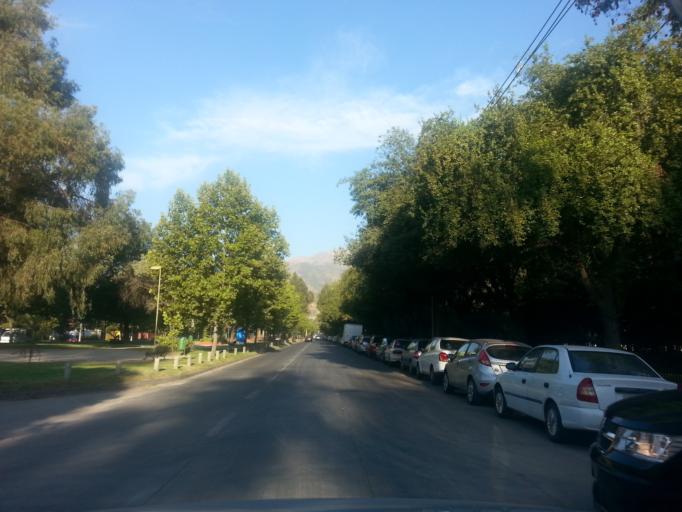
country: CL
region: Santiago Metropolitan
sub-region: Provincia de Santiago
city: Villa Presidente Frei, Nunoa, Santiago, Chile
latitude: -33.4300
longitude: -70.5476
